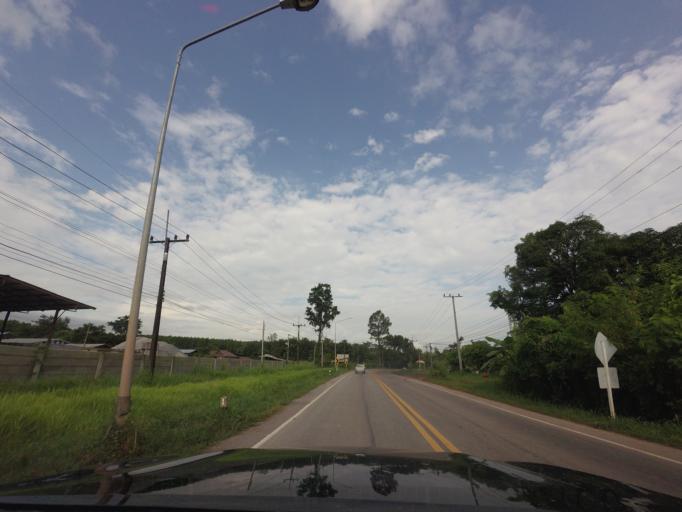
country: TH
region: Nong Khai
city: Pho Tak
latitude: 17.7806
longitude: 102.3790
